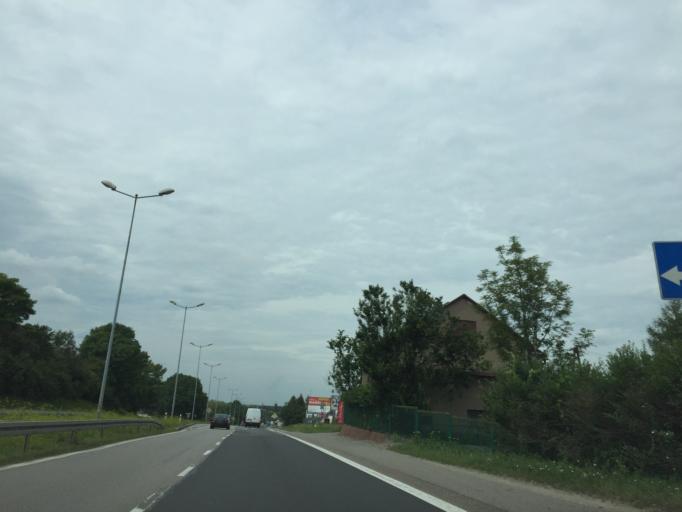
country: PL
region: Lesser Poland Voivodeship
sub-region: Powiat olkuski
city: Olkusz
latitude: 50.2794
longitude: 19.5755
